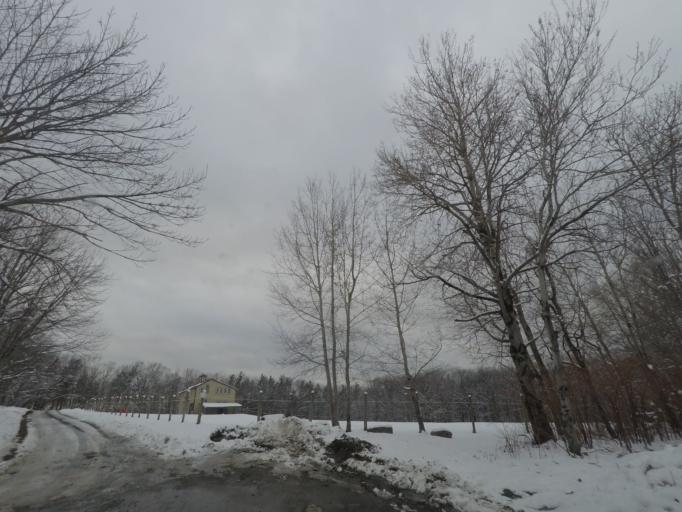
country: US
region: New York
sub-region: Rensselaer County
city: Averill Park
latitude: 42.6642
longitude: -73.5398
